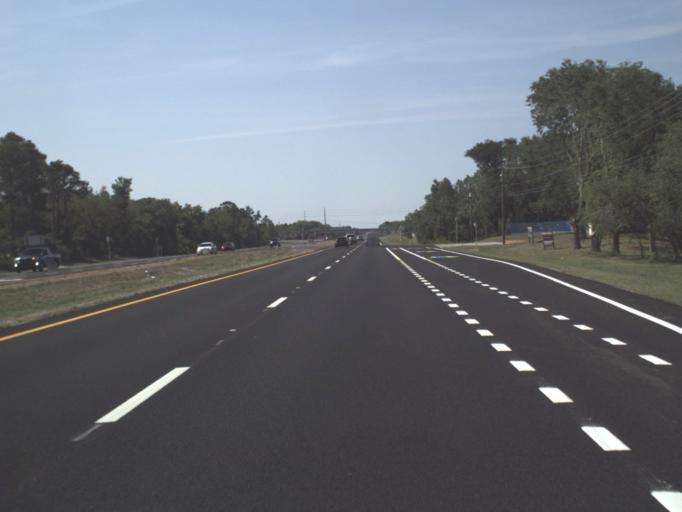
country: US
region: Florida
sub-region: Brevard County
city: Port Saint John
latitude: 28.5211
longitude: -80.7872
